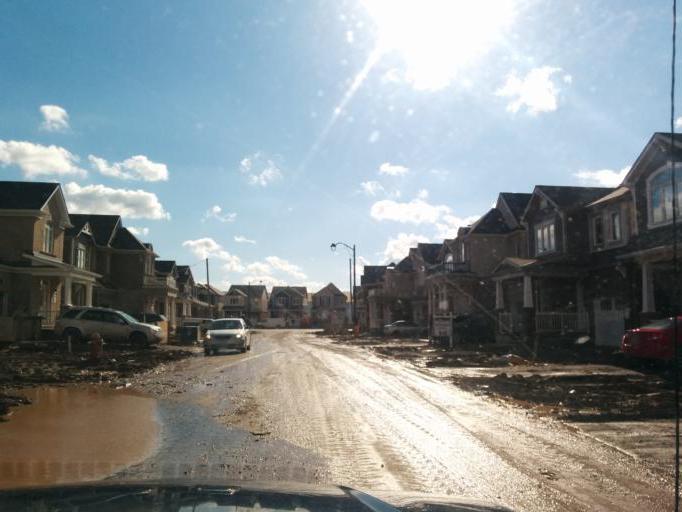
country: CA
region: Ontario
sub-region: Halton
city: Milton
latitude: 43.4861
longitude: -79.8390
